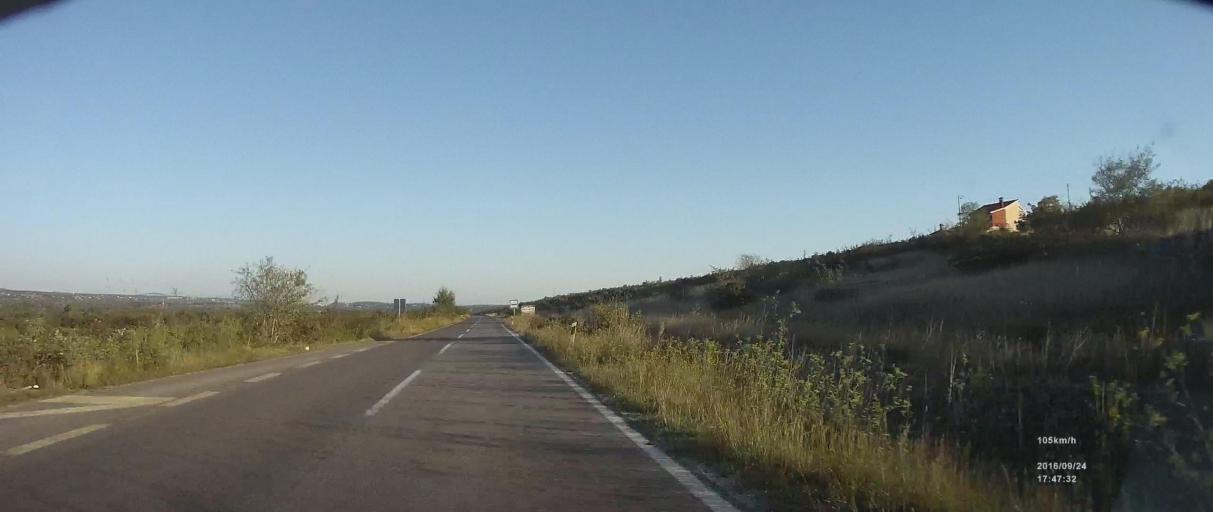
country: HR
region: Zadarska
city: Polaca
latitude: 44.0740
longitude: 15.5245
